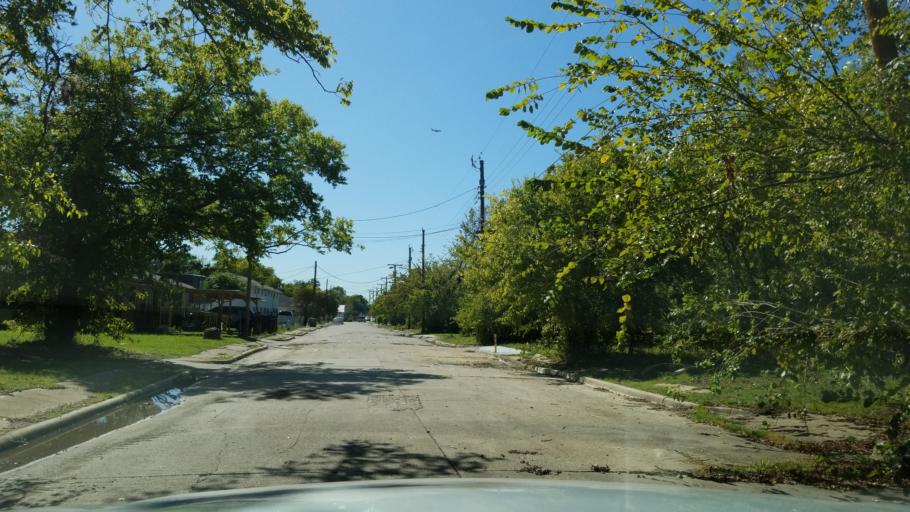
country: US
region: Texas
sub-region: Dallas County
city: Dallas
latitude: 32.7790
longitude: -96.7454
